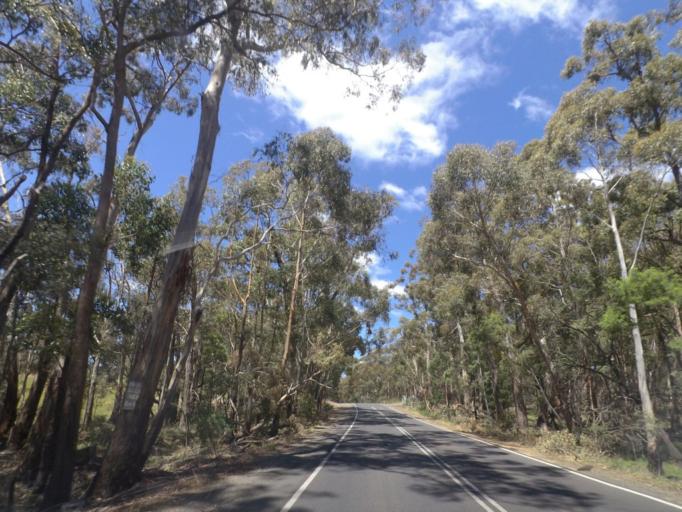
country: AU
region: Victoria
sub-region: Mount Alexander
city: Castlemaine
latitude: -37.2873
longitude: 144.2792
